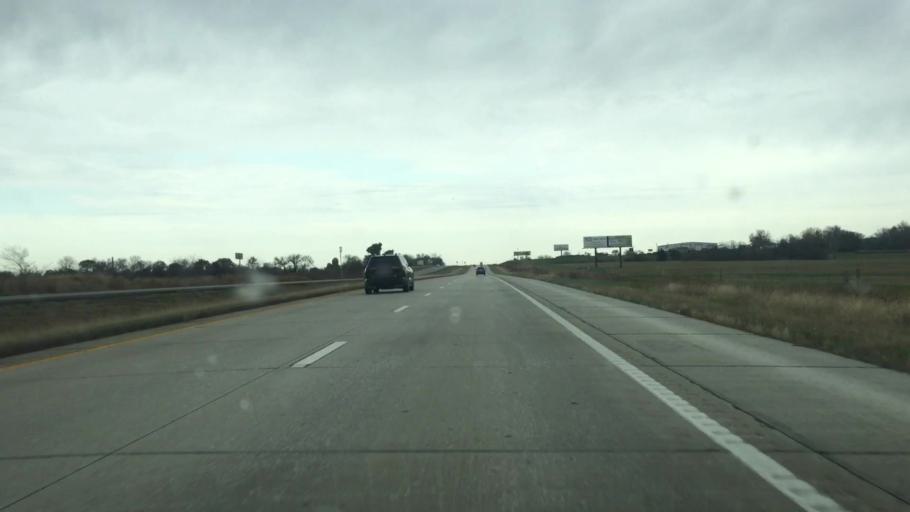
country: US
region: Missouri
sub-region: Saint Clair County
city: Osceola
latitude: 38.1604
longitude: -93.7224
